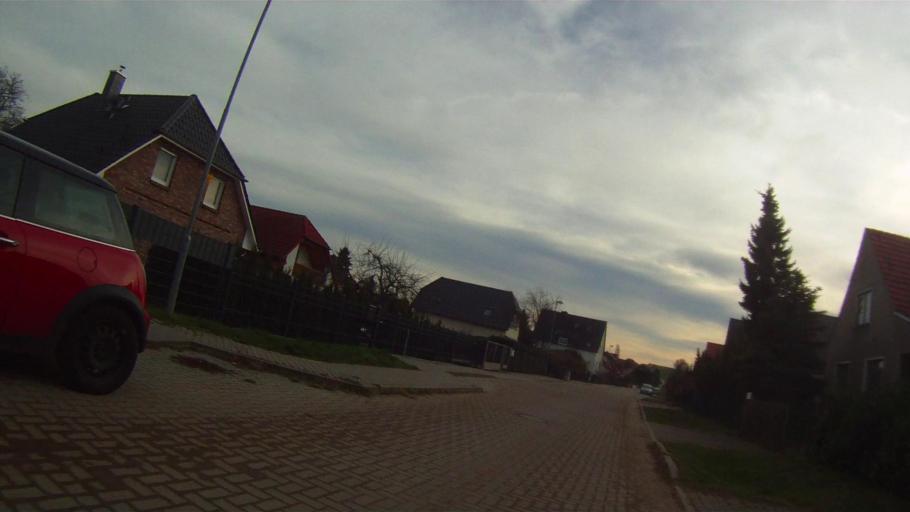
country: DE
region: Berlin
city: Buckow
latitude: 52.4178
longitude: 13.4513
